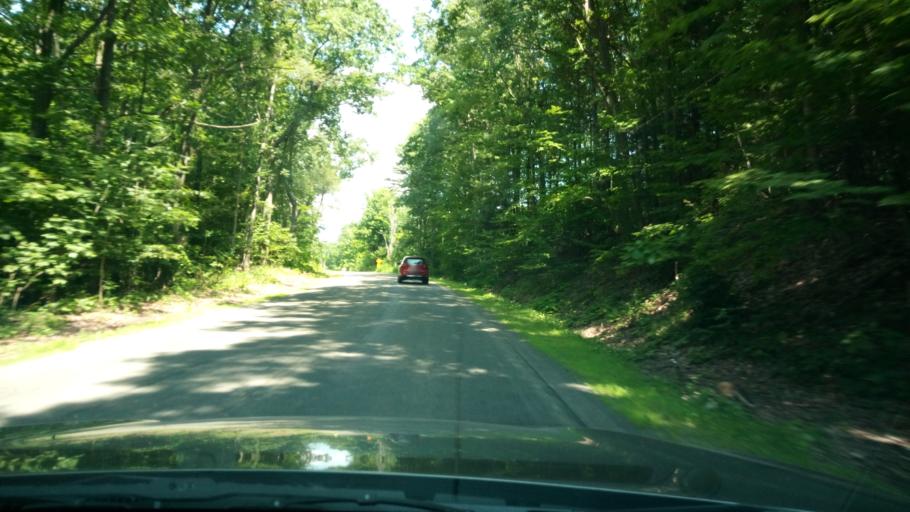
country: US
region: New York
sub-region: Chemung County
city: Horseheads North
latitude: 42.2667
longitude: -76.7990
